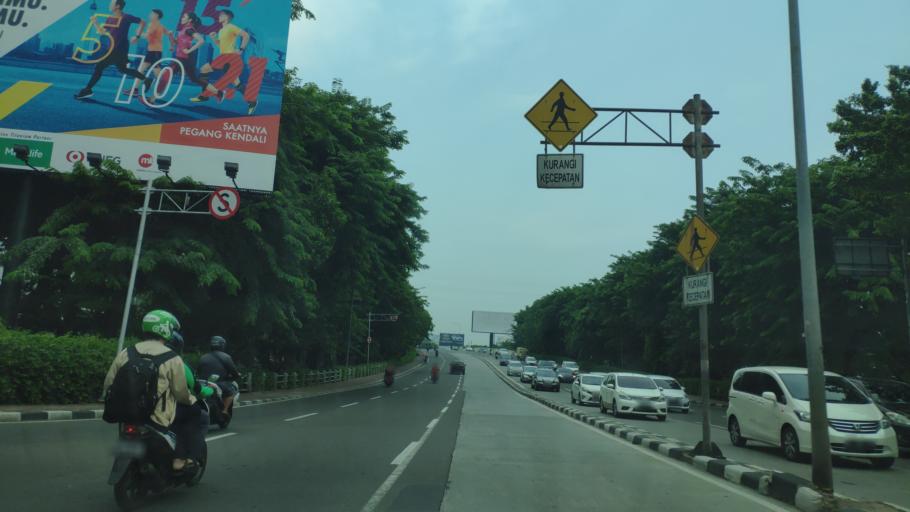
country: ID
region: Jakarta Raya
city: Jakarta
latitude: -6.1749
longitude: 106.8031
